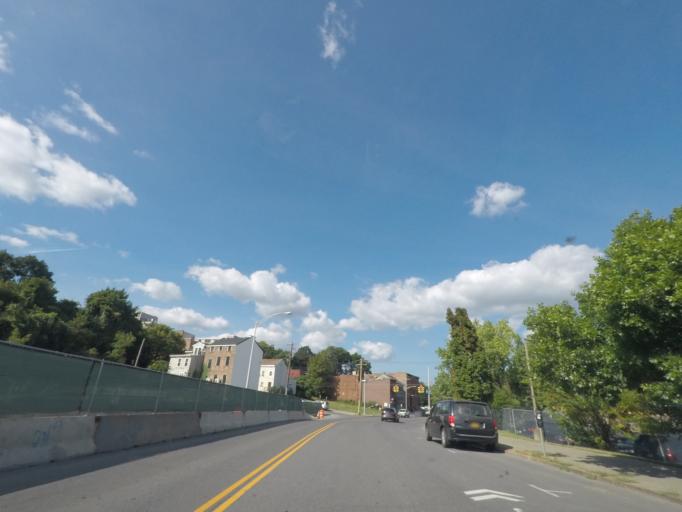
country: US
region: New York
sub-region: Albany County
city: Albany
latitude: 42.6570
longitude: -73.7484
